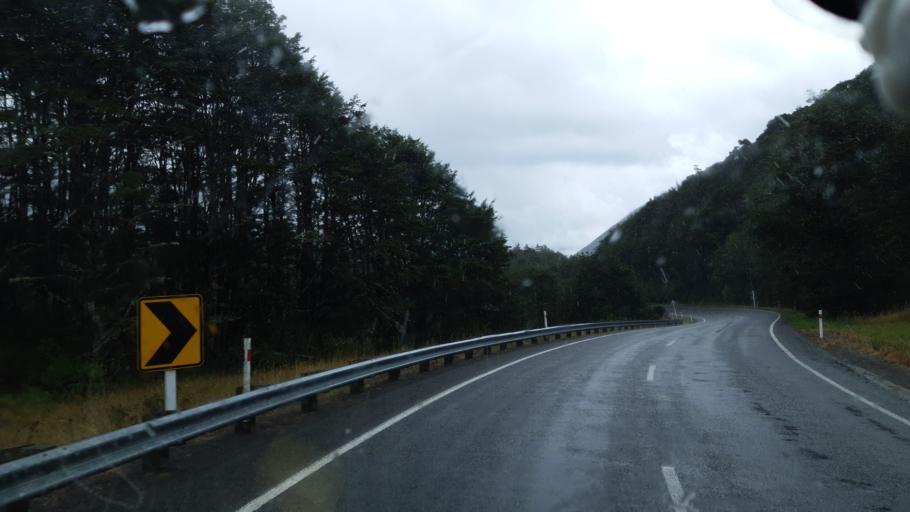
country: NZ
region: Canterbury
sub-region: Hurunui District
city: Amberley
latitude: -42.4301
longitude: 172.4016
